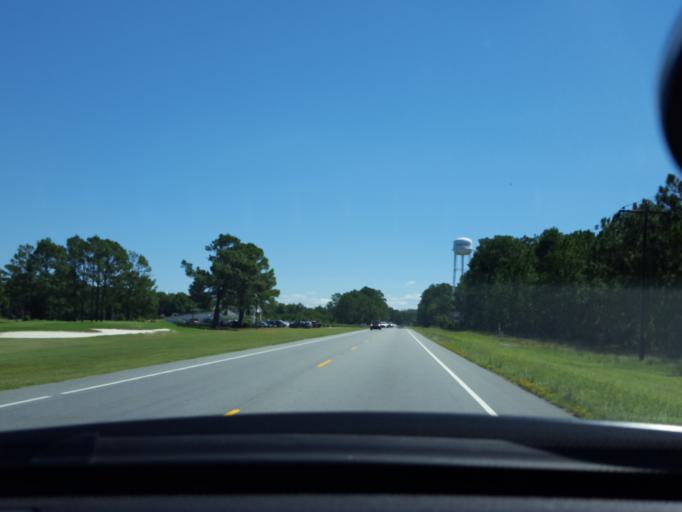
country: US
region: North Carolina
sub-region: Bladen County
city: Elizabethtown
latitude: 34.6497
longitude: -78.5367
